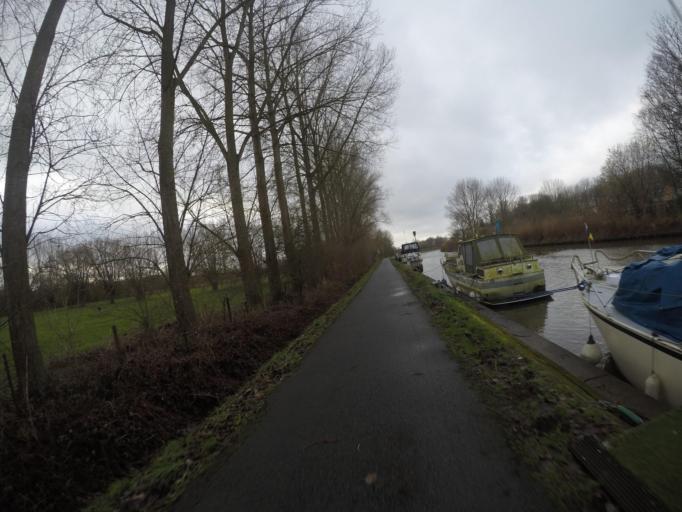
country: BE
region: Flanders
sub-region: Provincie Vlaams-Brabant
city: Liedekerke
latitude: 50.8722
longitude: 4.0754
